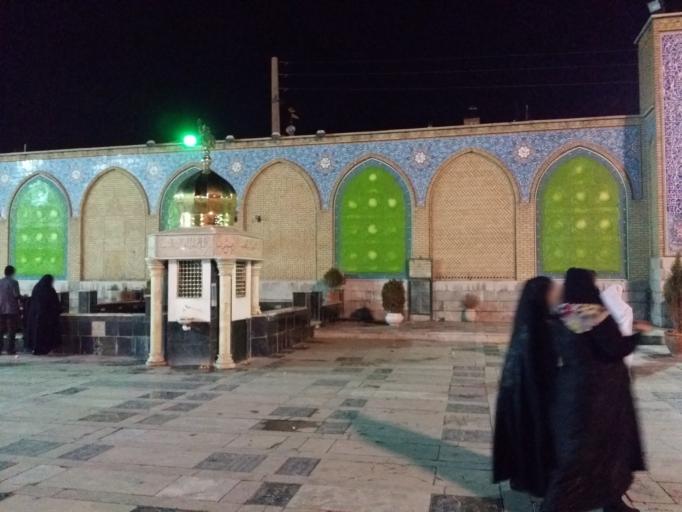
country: IR
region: Tehran
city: Pishva
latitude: 35.3030
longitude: 51.7292
